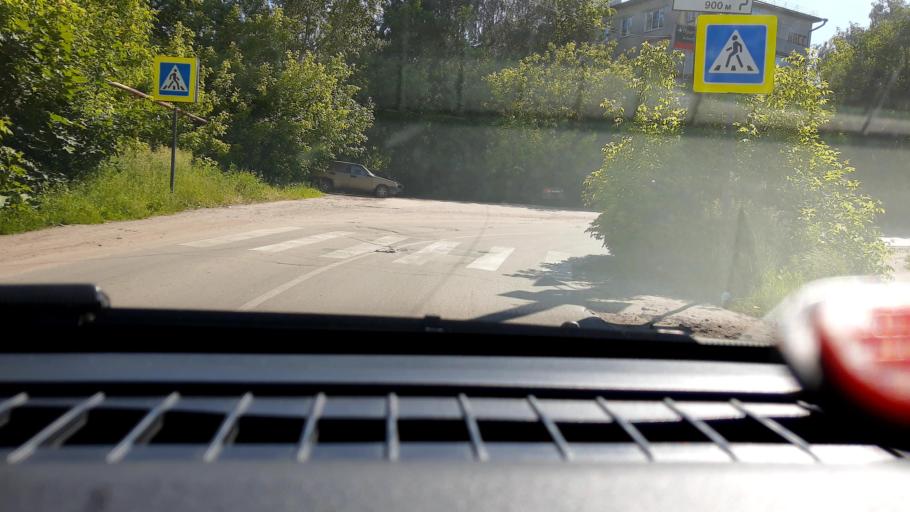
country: RU
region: Nizjnij Novgorod
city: Gidrotorf
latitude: 56.5226
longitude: 43.5463
